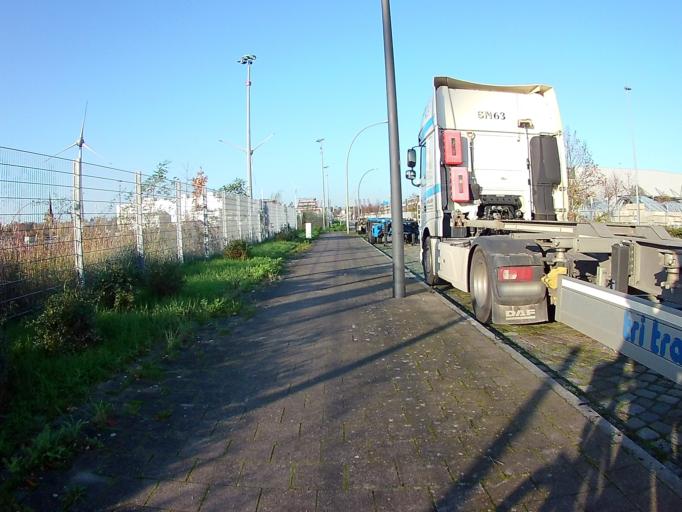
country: DE
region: Hamburg
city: Altona
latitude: 53.5029
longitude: 9.9217
